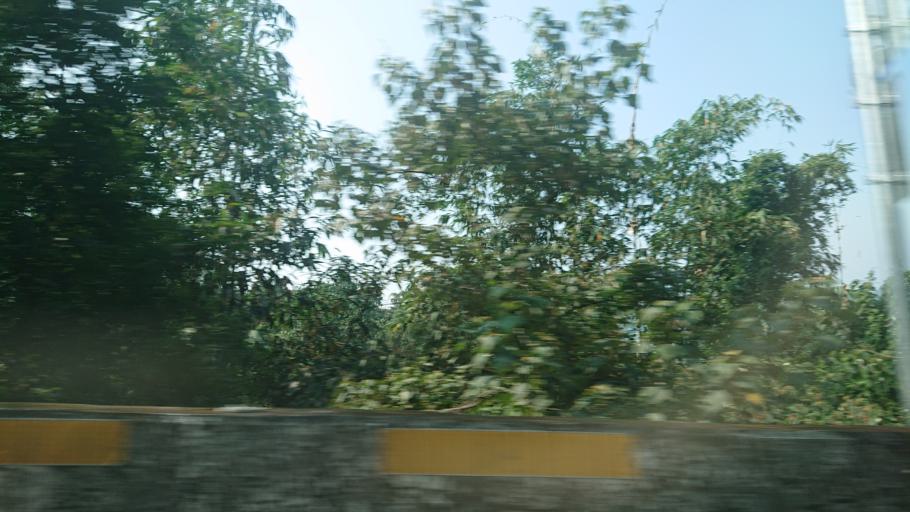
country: TW
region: Taiwan
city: Lugu
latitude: 23.7206
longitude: 120.6702
